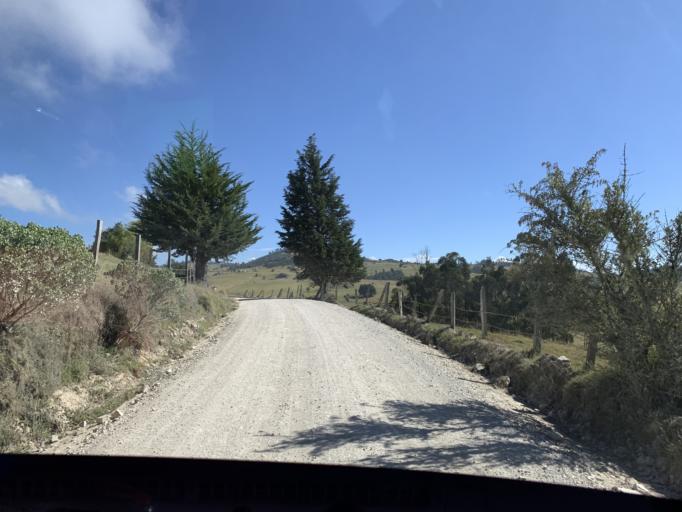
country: CO
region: Boyaca
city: Tuta
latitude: 5.6762
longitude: -73.1466
